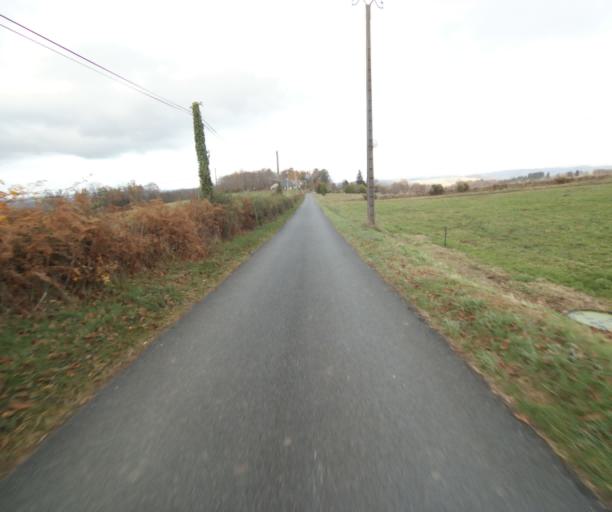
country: FR
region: Limousin
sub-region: Departement de la Correze
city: Sainte-Fortunade
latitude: 45.2172
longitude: 1.7906
